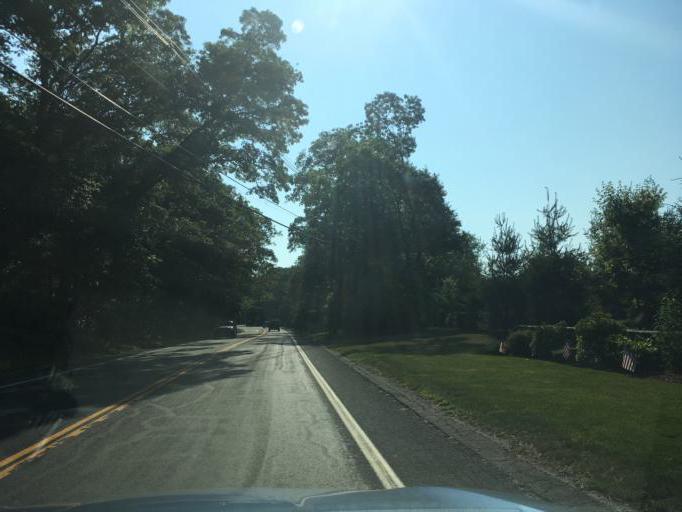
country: US
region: Rhode Island
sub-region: Washington County
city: Kingston
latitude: 41.4826
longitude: -71.5044
